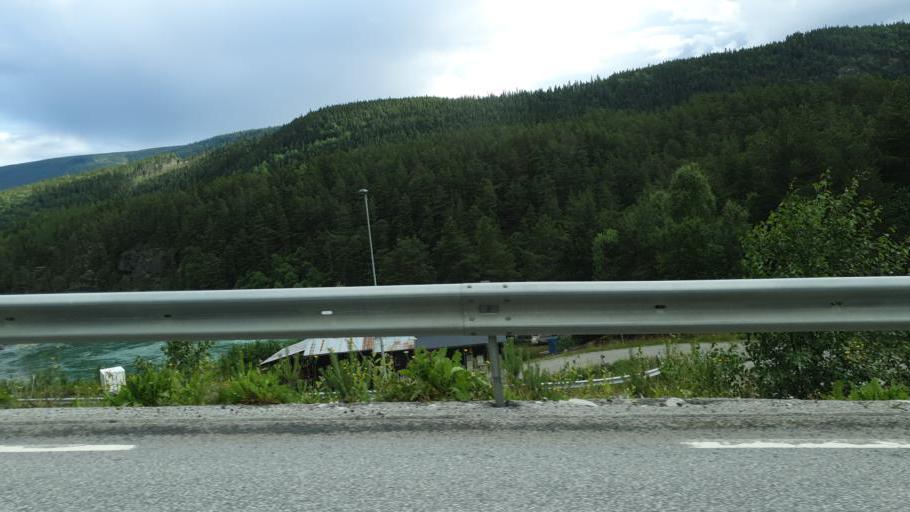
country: NO
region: Oppland
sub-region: Vaga
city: Vagamo
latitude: 61.8740
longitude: 9.1866
